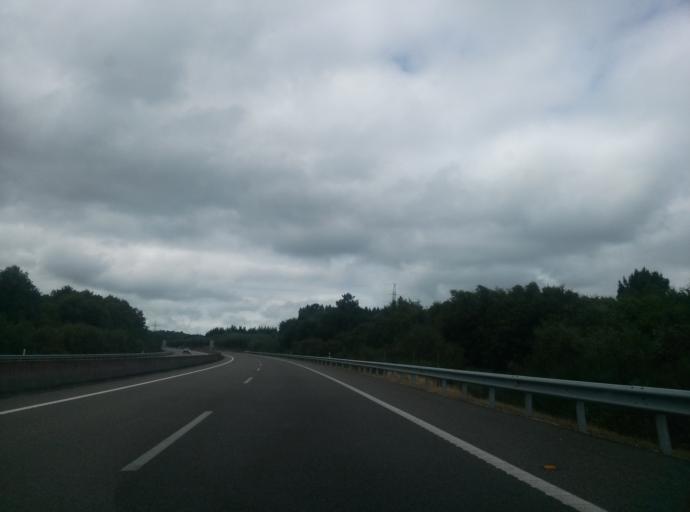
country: ES
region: Galicia
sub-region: Provincia de Lugo
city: Vilalba
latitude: 43.3239
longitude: -7.6934
